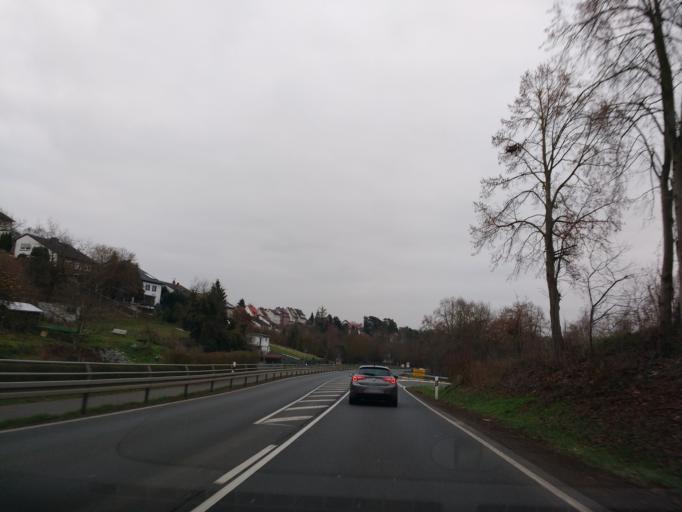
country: DE
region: Hesse
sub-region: Regierungsbezirk Kassel
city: Baunatal
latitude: 51.2162
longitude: 9.4349
